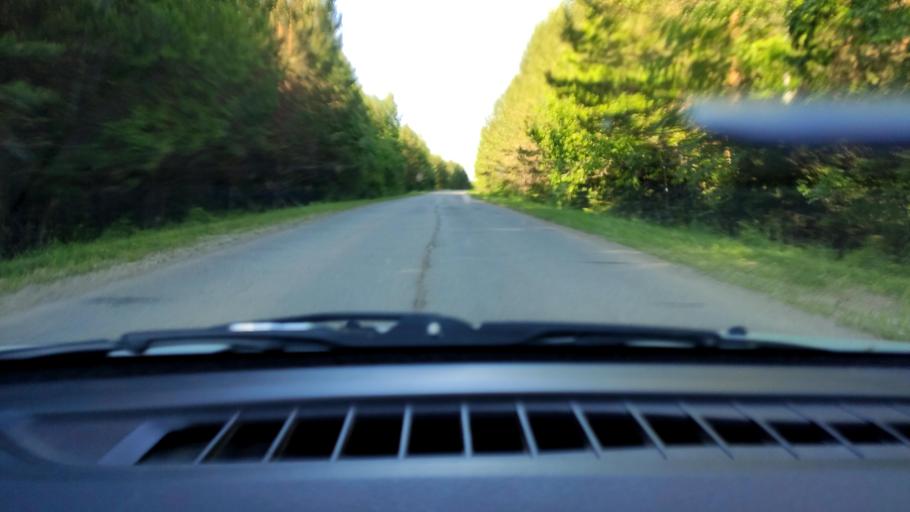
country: RU
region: Perm
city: Uinskoye
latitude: 57.0834
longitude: 56.6185
